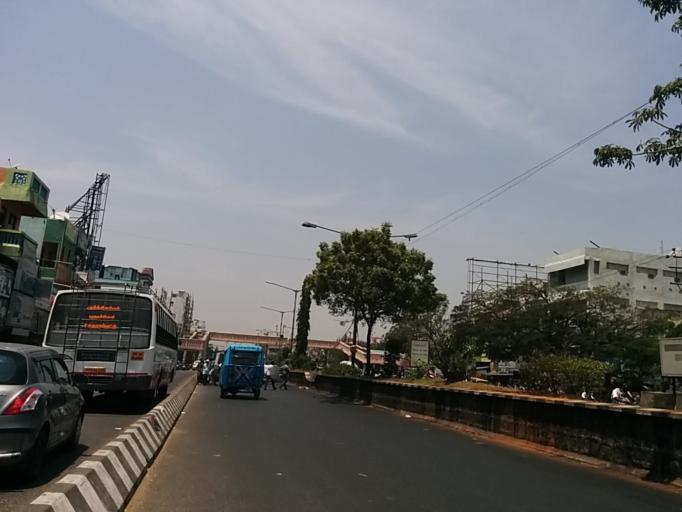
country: IN
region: Pondicherry
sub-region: Puducherry
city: Puducherry
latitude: 11.9316
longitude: 79.8172
